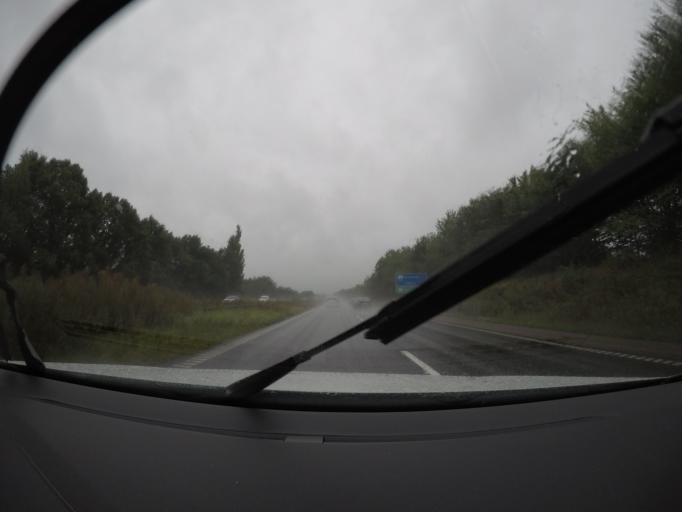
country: DK
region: Capital Region
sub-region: Fredensborg Kommune
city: Kokkedal
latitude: 55.9218
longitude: 12.4745
